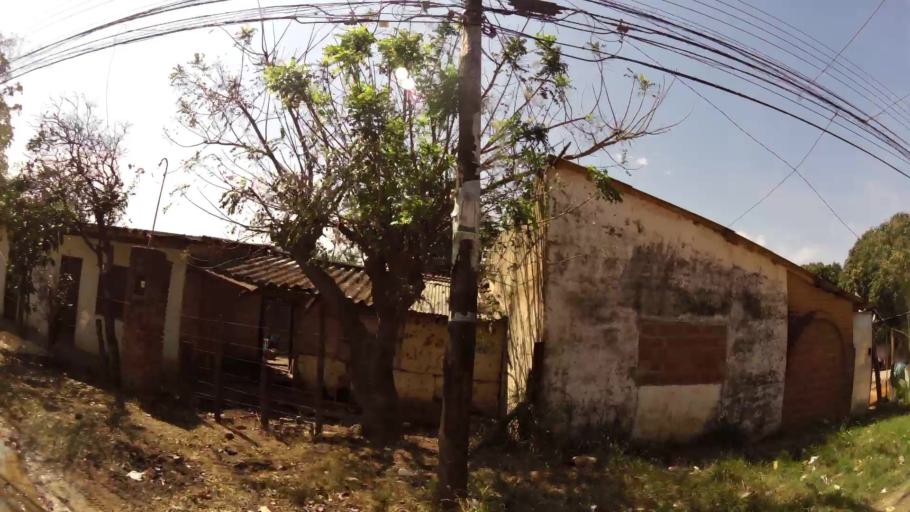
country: BO
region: Santa Cruz
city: Santa Cruz de la Sierra
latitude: -17.7384
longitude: -63.1490
